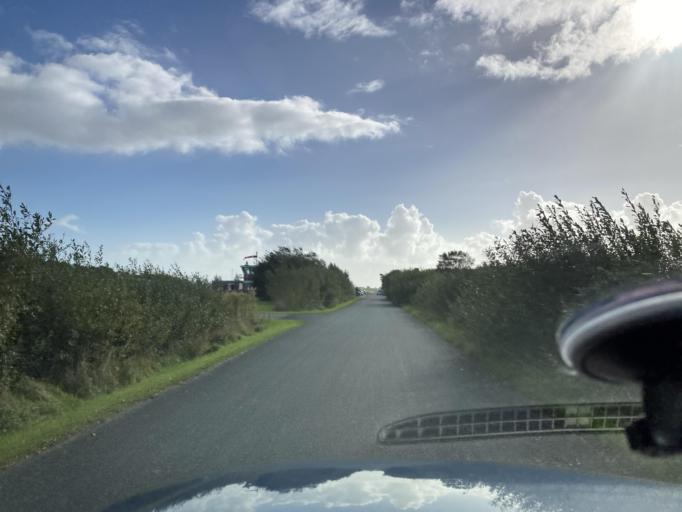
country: DE
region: Schleswig-Holstein
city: Oesterdeichstrich
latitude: 54.1551
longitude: 8.8952
